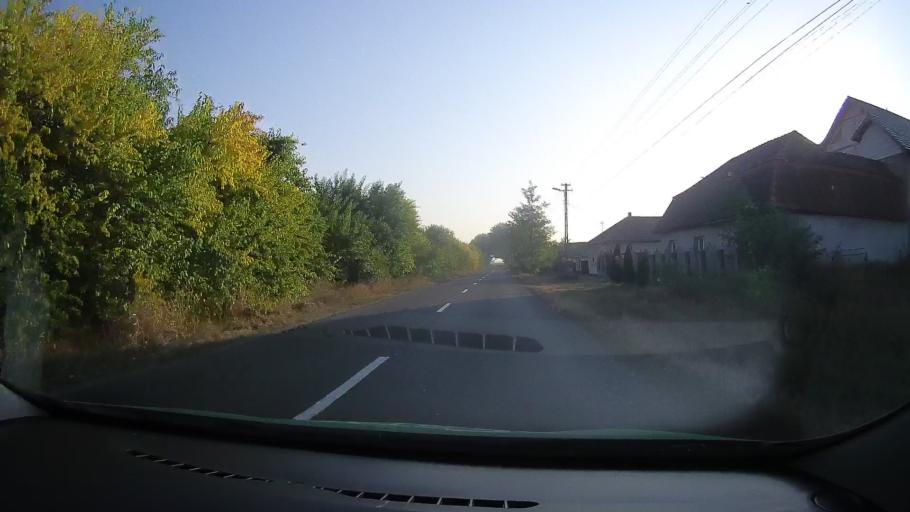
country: RO
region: Arad
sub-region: Comuna Curtici
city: Curtici
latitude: 46.3482
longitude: 21.3288
